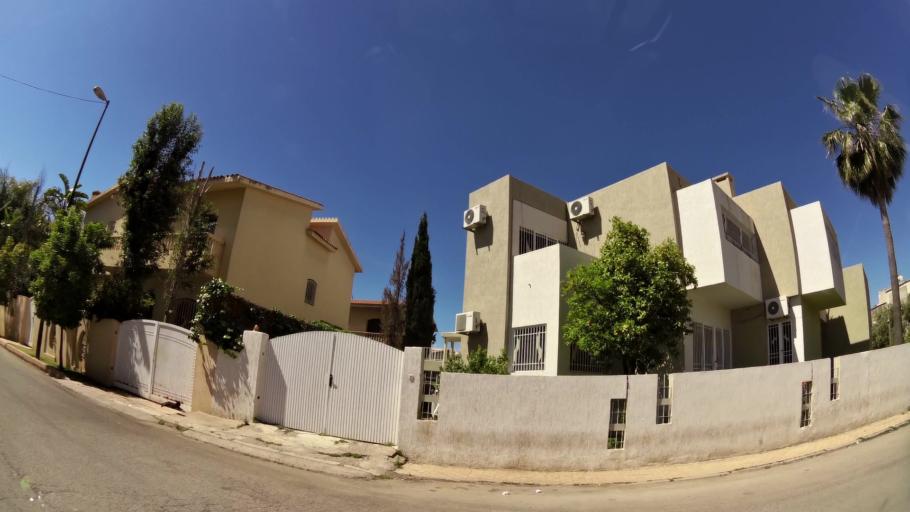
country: MA
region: Fes-Boulemane
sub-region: Fes
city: Fes
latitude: 34.0160
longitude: -4.9976
